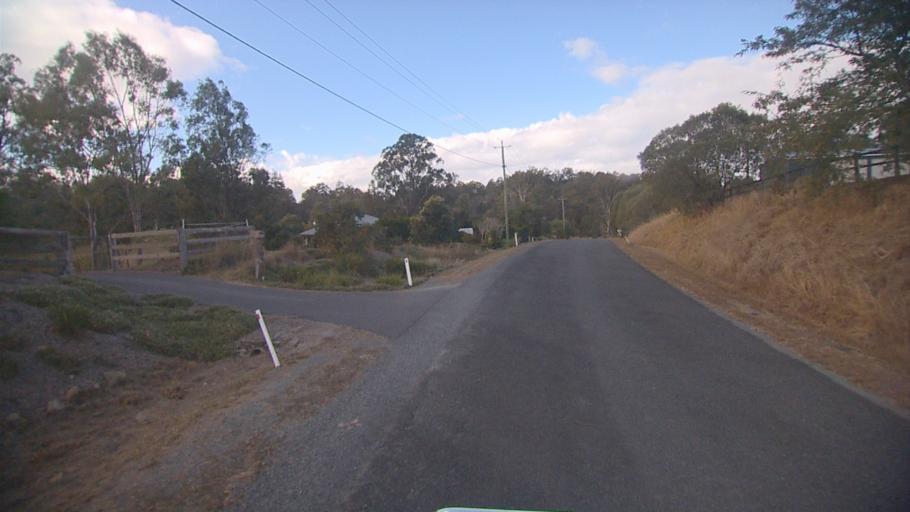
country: AU
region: Queensland
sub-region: Logan
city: Cedar Vale
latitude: -27.9027
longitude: 153.0669
